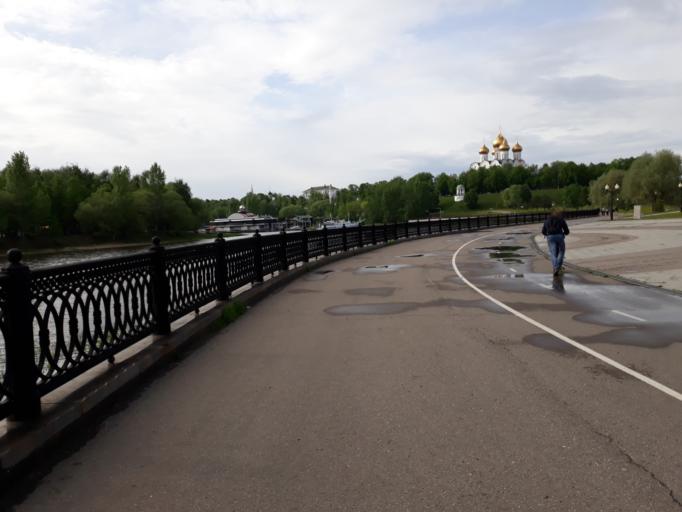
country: RU
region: Jaroslavl
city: Yaroslavl
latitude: 57.6181
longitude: 39.9033
